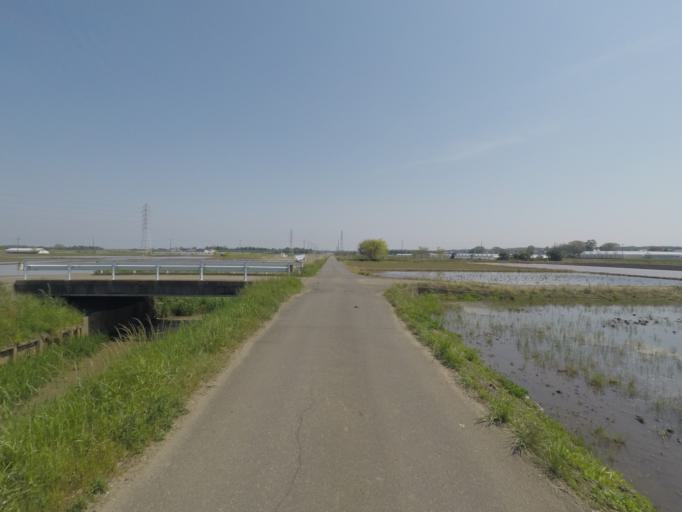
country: JP
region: Ibaraki
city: Naka
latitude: 36.1005
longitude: 140.1590
